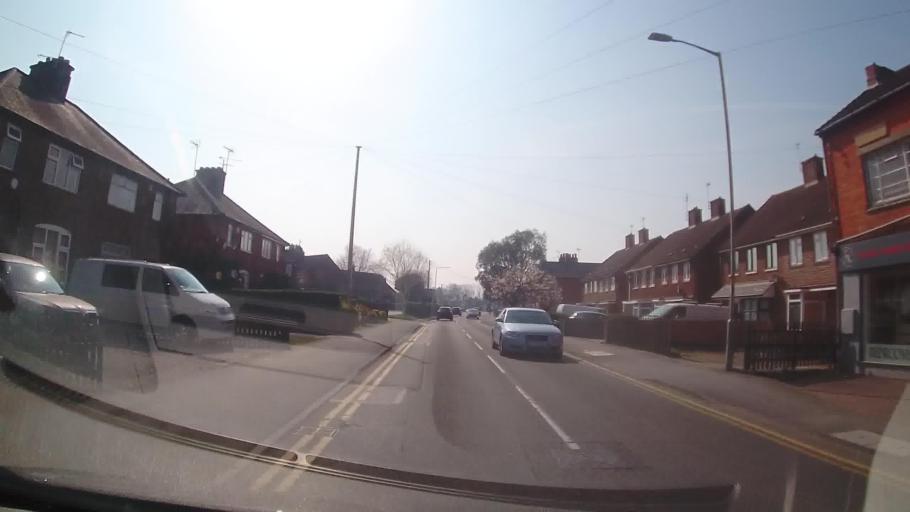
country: GB
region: England
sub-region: Leicestershire
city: Glenfield
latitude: 52.6528
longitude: -1.2007
